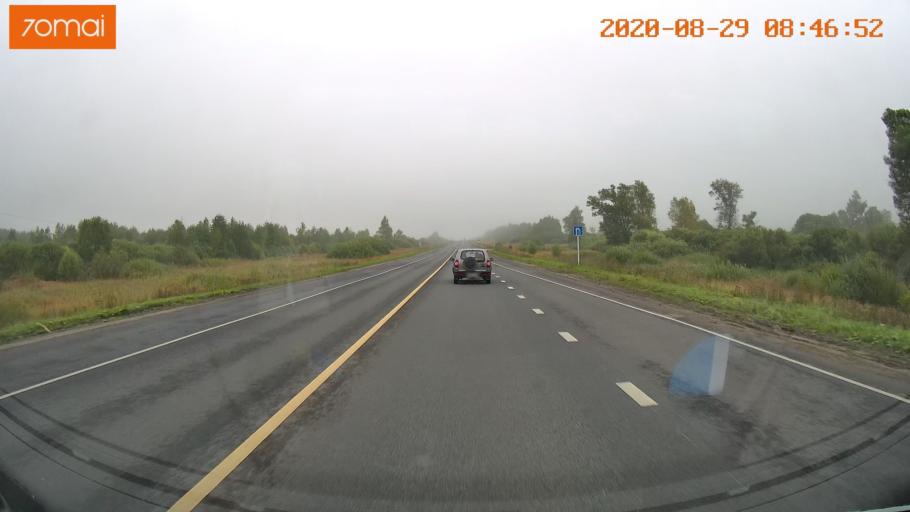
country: RU
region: Ivanovo
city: Rodniki
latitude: 57.1445
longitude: 41.8233
